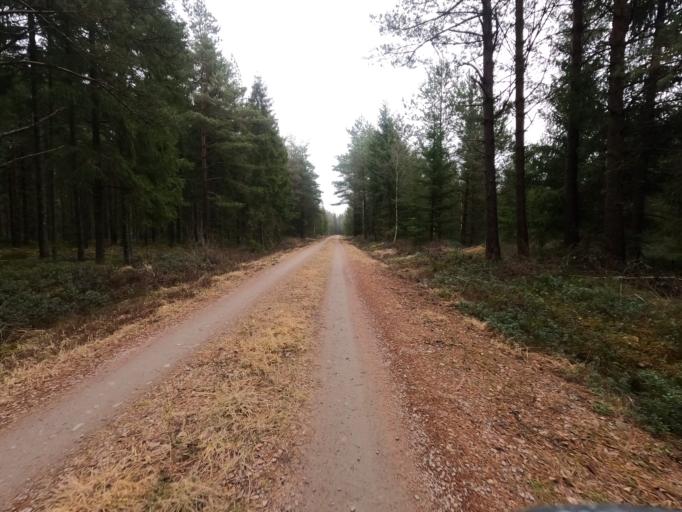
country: SE
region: Kronoberg
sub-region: Markaryds Kommun
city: Stromsnasbruk
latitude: 56.7931
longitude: 13.6102
